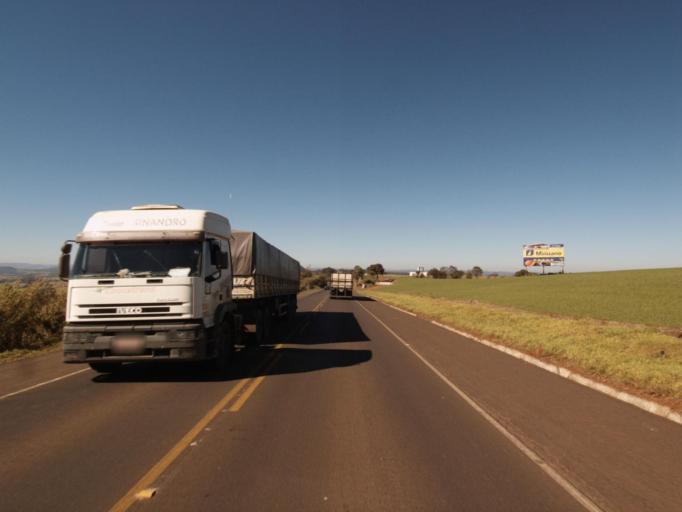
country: BR
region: Santa Catarina
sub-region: Chapeco
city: Chapeco
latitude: -26.8706
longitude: -52.9603
